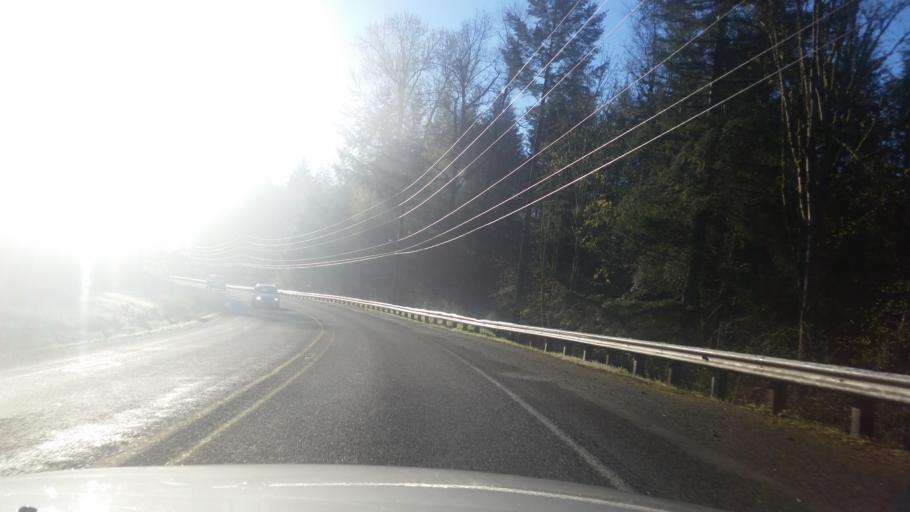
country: US
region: Washington
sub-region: Pierce County
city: Eatonville
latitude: 46.8737
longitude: -122.2971
